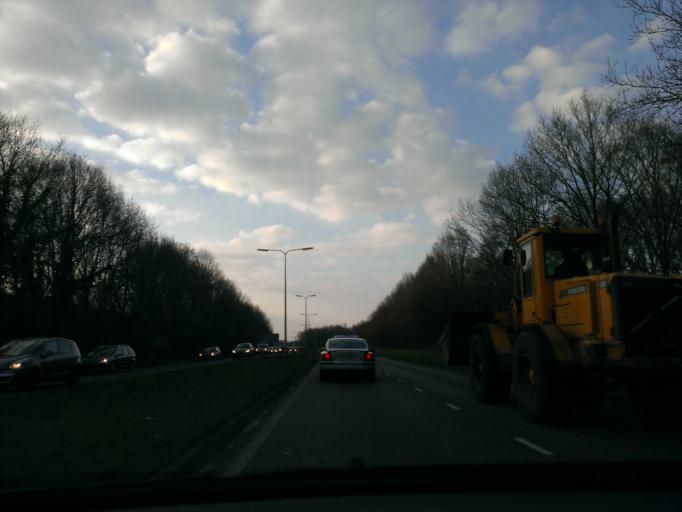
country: NL
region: Overijssel
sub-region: Gemeente Zwolle
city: Zwolle
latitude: 52.4950
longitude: 6.1127
